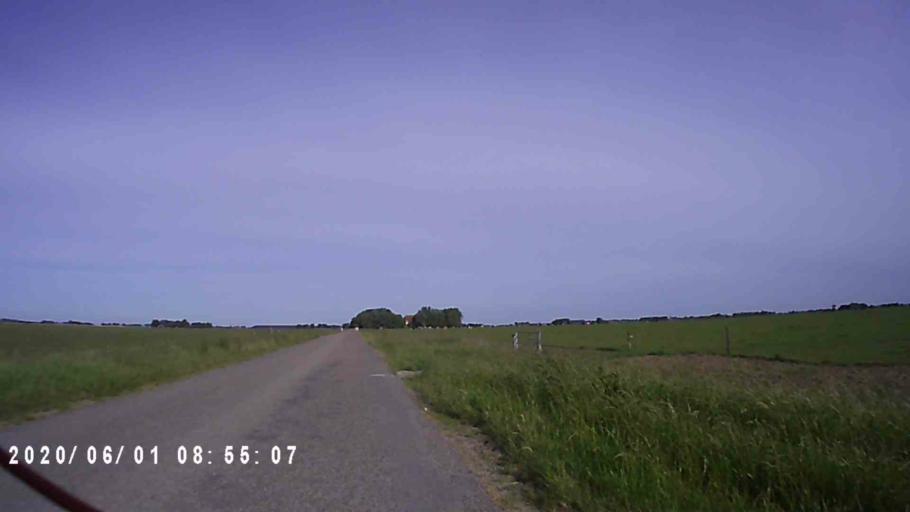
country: NL
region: Friesland
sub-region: Gemeente Leeuwarderadeel
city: Britsum
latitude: 53.2781
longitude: 5.8257
